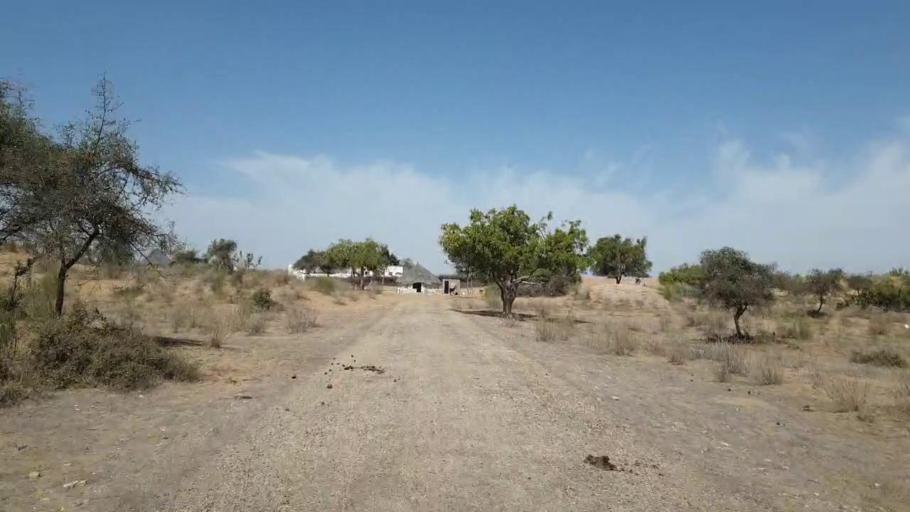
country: PK
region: Sindh
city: Nabisar
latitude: 25.0929
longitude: 69.9901
